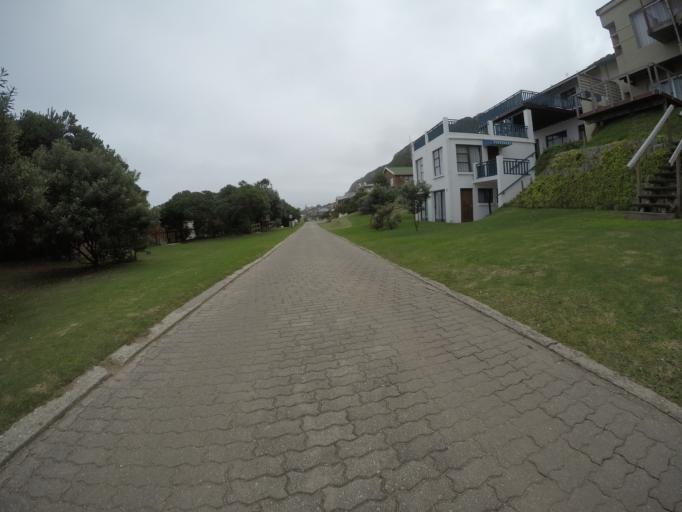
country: ZA
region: Eastern Cape
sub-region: Cacadu District Municipality
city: Kareedouw
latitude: -34.0711
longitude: 24.2188
